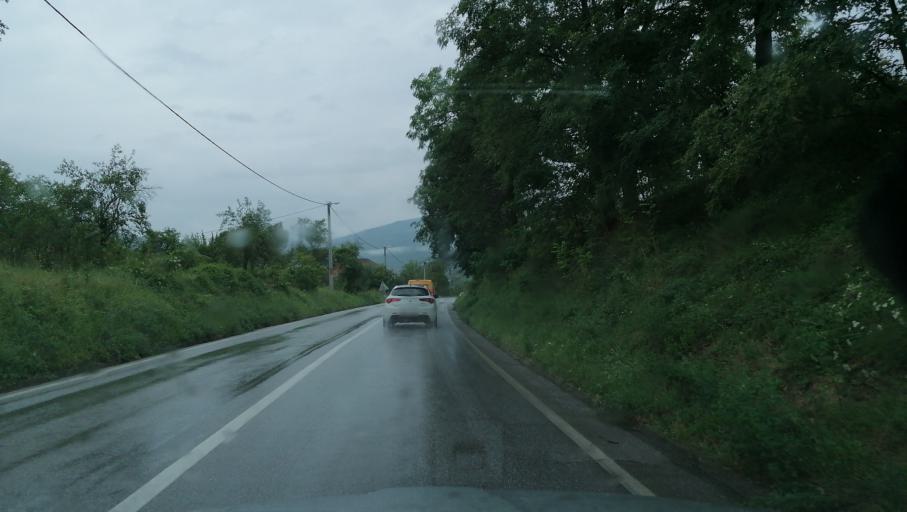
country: BA
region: Federation of Bosnia and Herzegovina
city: Gorazde
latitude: 43.6763
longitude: 19.0398
